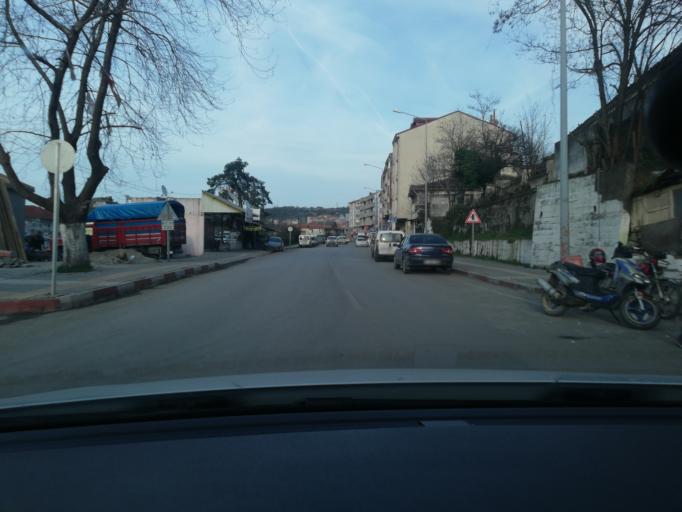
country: TR
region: Zonguldak
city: Tieum
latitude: 41.5604
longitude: 32.0232
